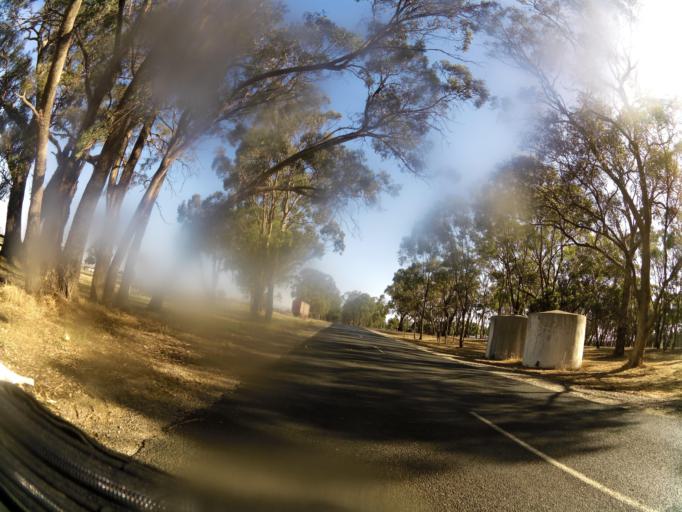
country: AU
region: Victoria
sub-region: Murrindindi
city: Kinglake West
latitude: -36.9620
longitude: 145.1080
